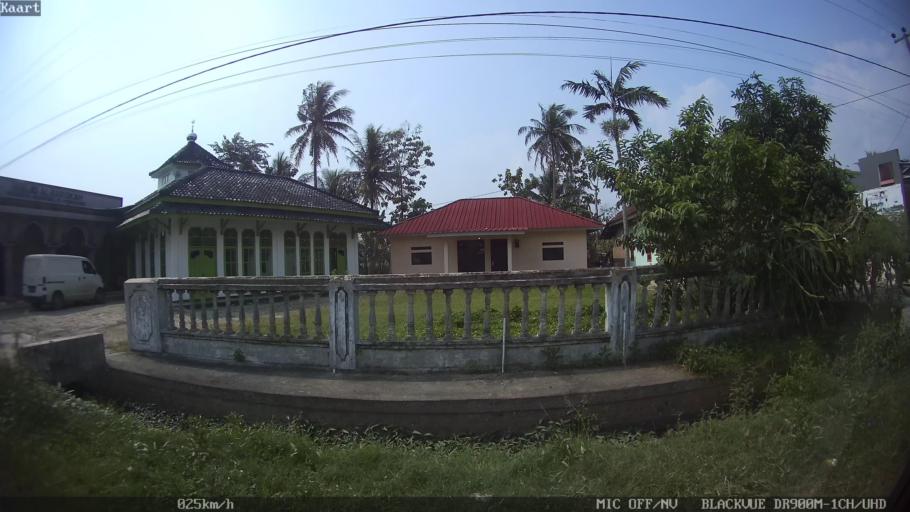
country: ID
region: Lampung
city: Kedondong
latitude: -5.4099
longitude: 104.9988
